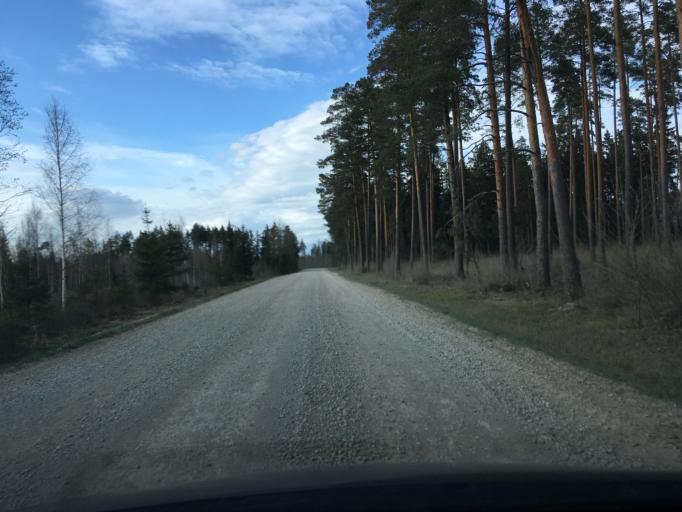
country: EE
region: Raplamaa
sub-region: Maerjamaa vald
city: Marjamaa
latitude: 58.9552
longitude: 24.3255
